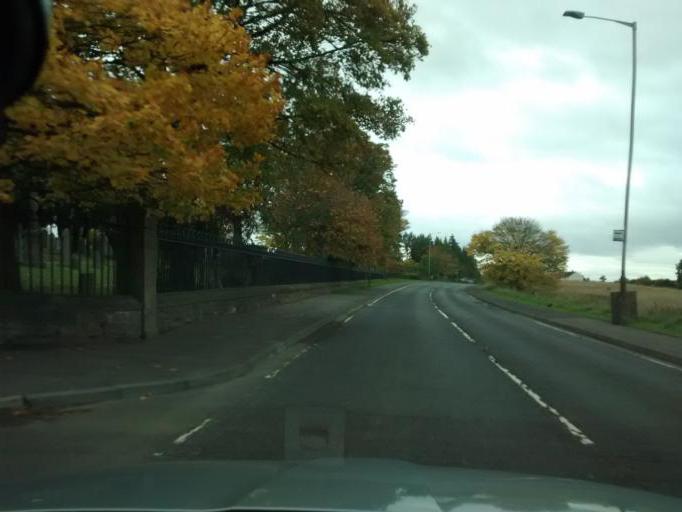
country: GB
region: Scotland
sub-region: Perth and Kinross
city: Blairgowrie
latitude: 56.5796
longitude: -3.3458
